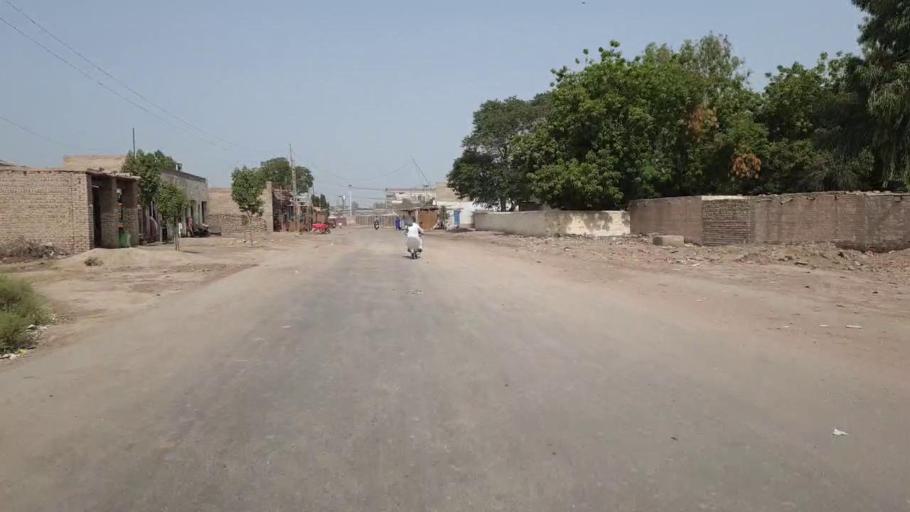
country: PK
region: Sindh
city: Daulatpur
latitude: 26.5590
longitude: 67.9831
